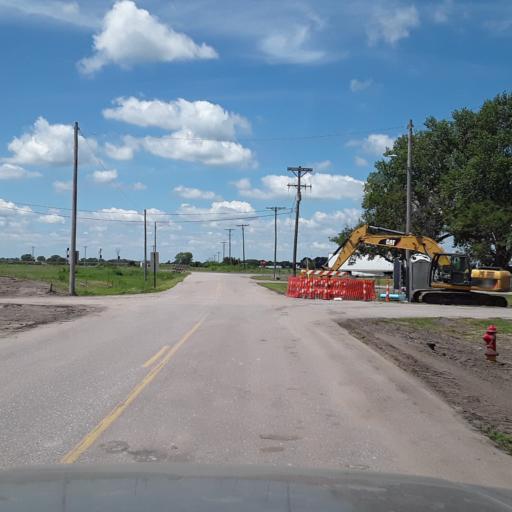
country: US
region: Nebraska
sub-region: Merrick County
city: Central City
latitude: 41.1048
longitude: -98.0195
